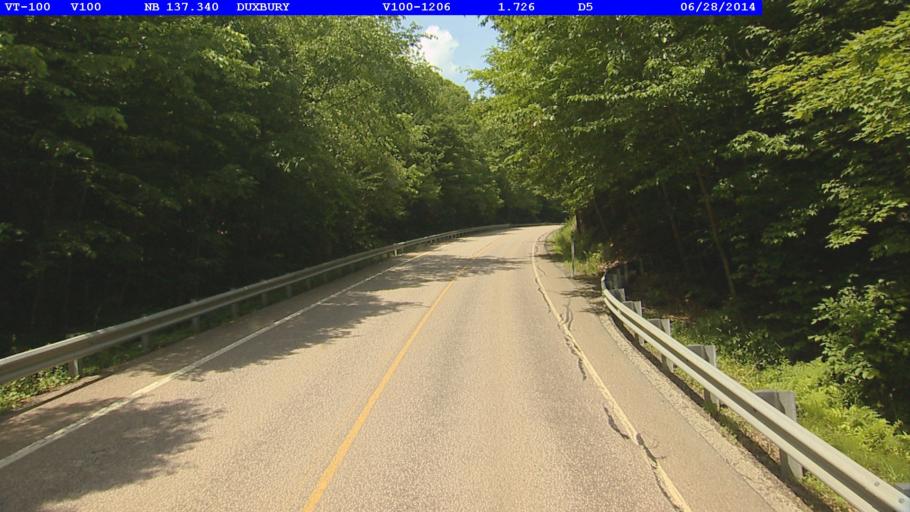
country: US
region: Vermont
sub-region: Washington County
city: Waterbury
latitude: 44.2707
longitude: -72.7856
